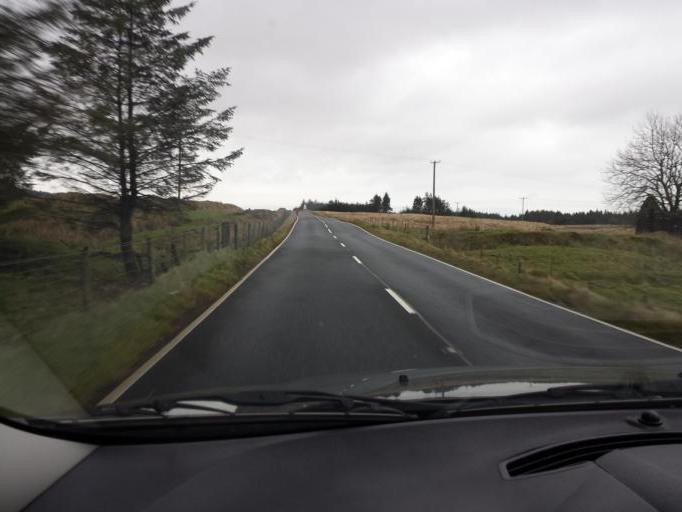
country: GB
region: Northern Ireland
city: Glenariff
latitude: 55.0072
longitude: -6.1524
